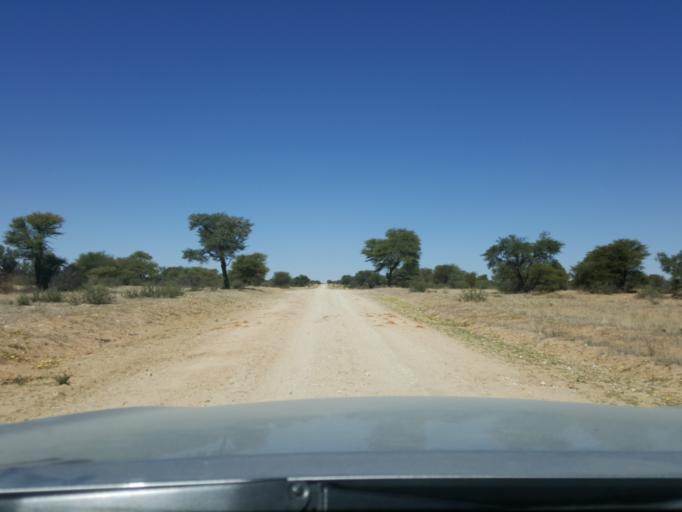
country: BW
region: Kgalagadi
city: Hukuntsi
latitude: -24.0648
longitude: 21.2235
